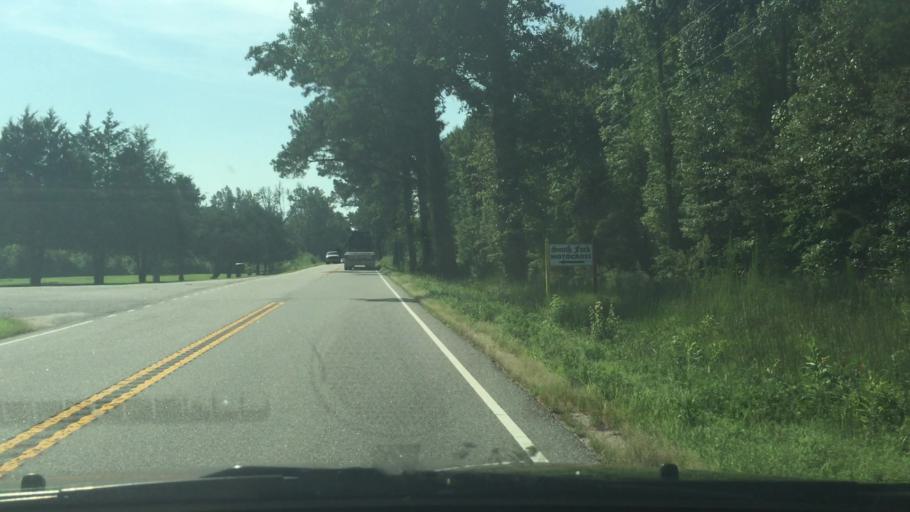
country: US
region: Virginia
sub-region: Sussex County
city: Sussex
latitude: 37.0179
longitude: -77.2834
